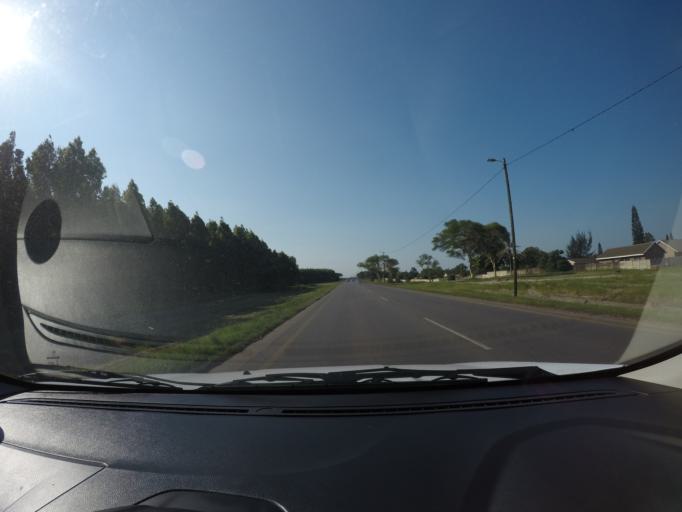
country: ZA
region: KwaZulu-Natal
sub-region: uThungulu District Municipality
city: Richards Bay
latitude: -28.7190
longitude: 32.0325
